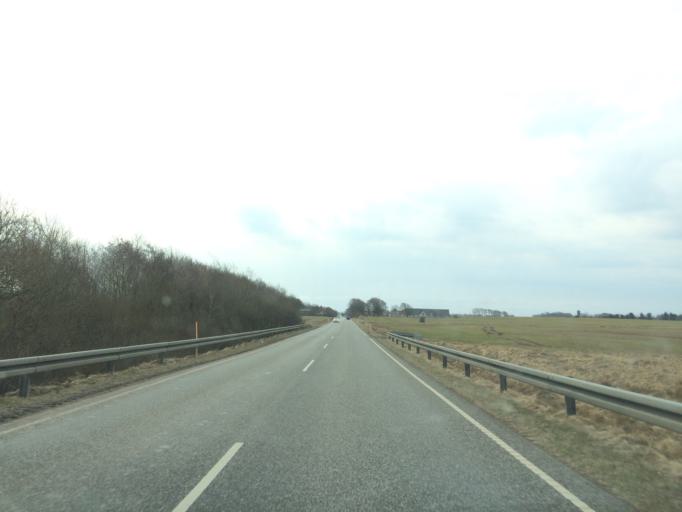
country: DK
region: Central Jutland
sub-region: Ringkobing-Skjern Kommune
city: Skjern
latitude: 56.0666
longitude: 8.5055
